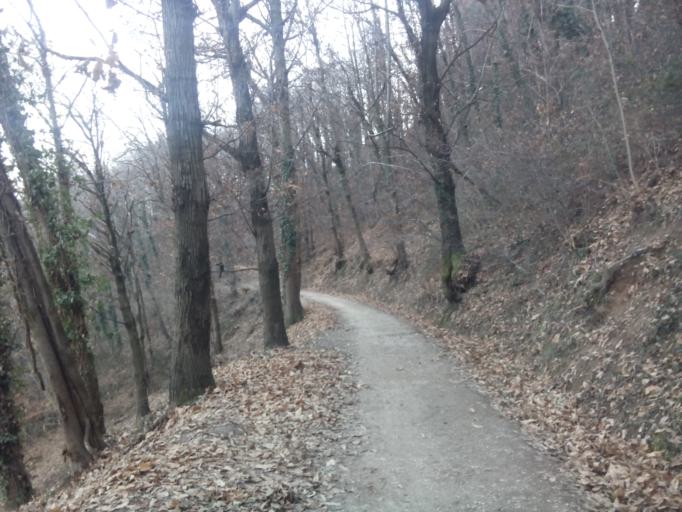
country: IT
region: Veneto
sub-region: Provincia di Padova
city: Galzignano
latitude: 45.3187
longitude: 11.7137
